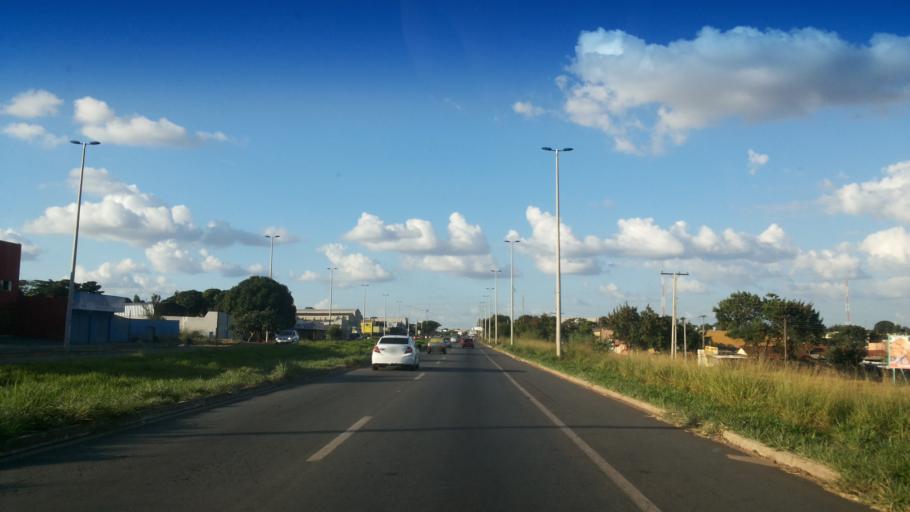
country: BR
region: Goias
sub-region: Aparecida De Goiania
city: Aparecida de Goiania
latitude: -16.7583
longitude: -49.3422
